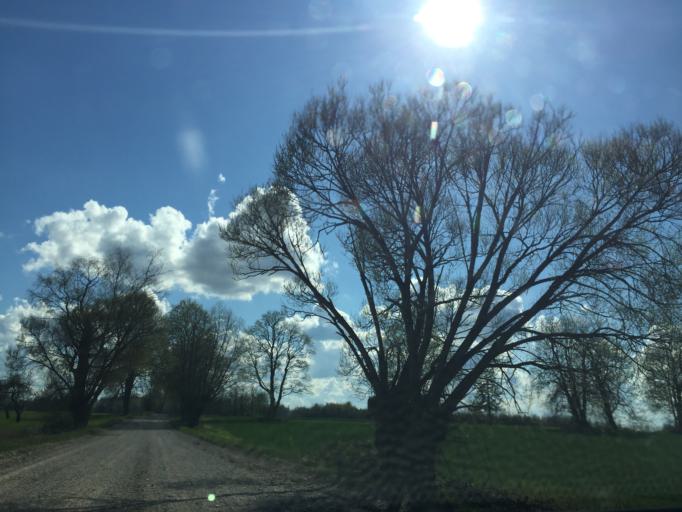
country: LV
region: Strenci
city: Strenci
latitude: 57.4891
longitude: 25.6362
